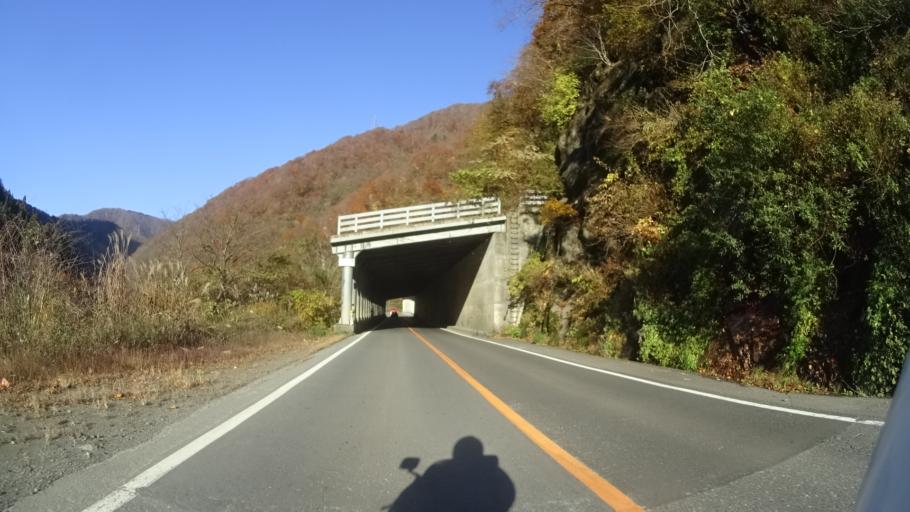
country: JP
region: Fukui
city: Ono
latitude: 35.9313
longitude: 136.6362
